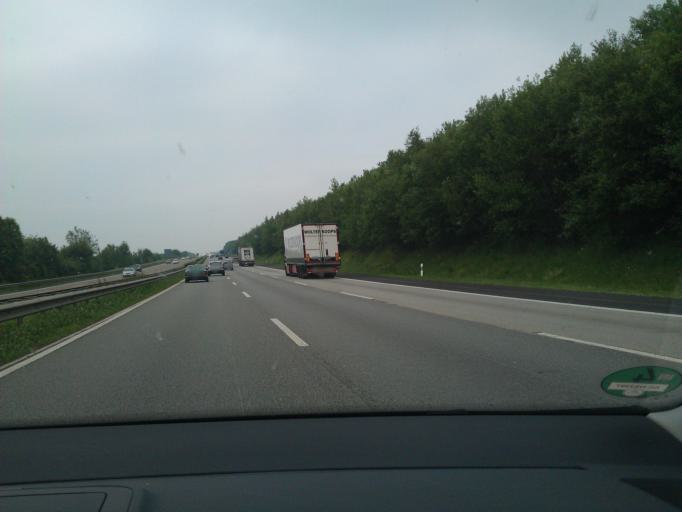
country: DE
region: Rheinland-Pfalz
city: Gorgeshausen
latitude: 50.4133
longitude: 7.9516
